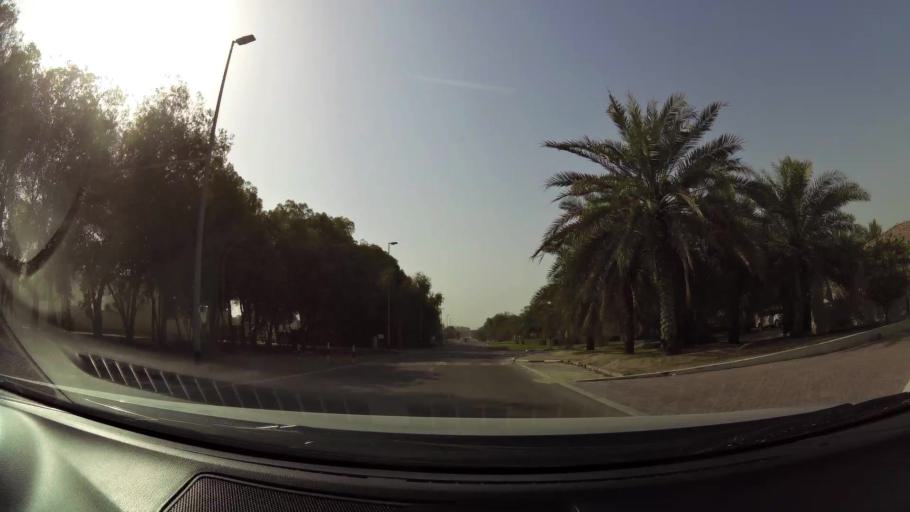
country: AE
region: Dubai
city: Dubai
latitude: 25.1469
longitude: 55.3225
